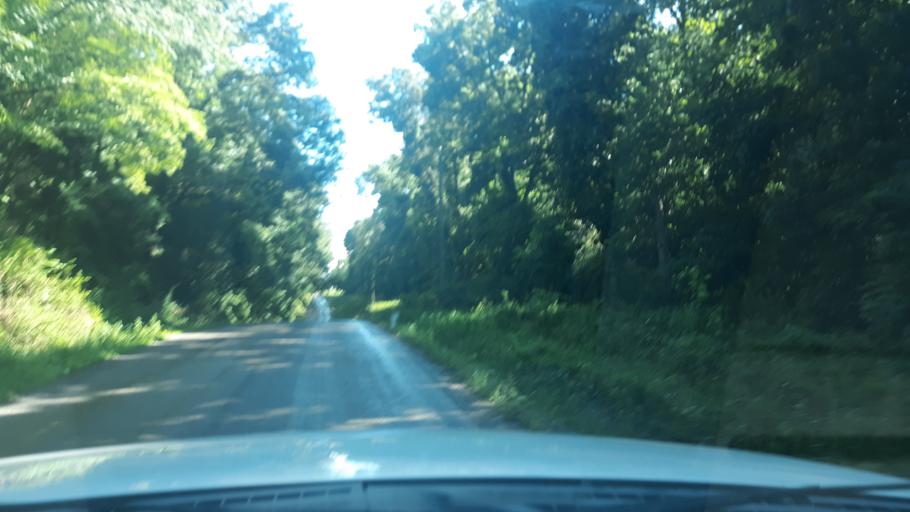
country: US
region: Illinois
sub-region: Saline County
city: Harrisburg
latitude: 37.8504
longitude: -88.5814
